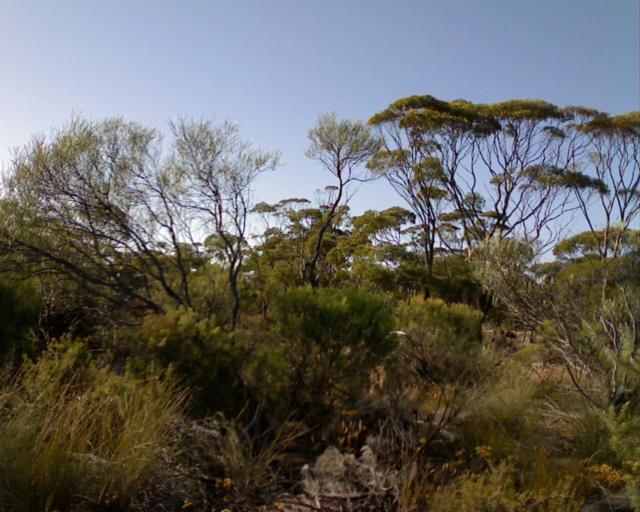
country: AU
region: Western Australia
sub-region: Wongan-Ballidu
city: Wongan Hills
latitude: -30.2877
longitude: 116.9689
